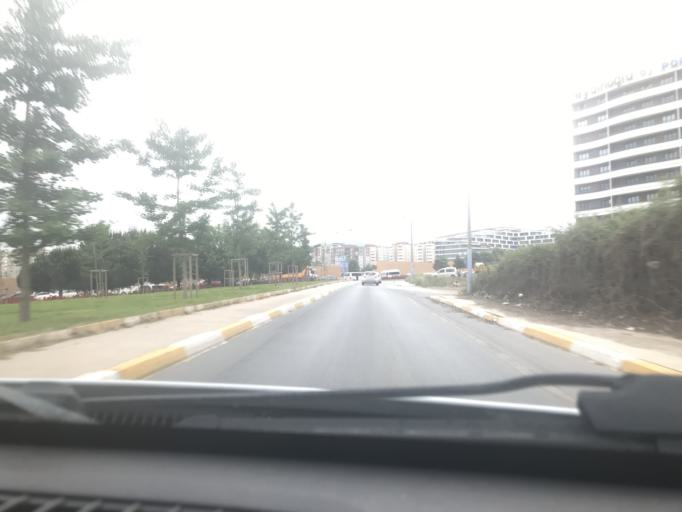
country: TR
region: Istanbul
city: Sultanbeyli
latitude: 40.9256
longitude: 29.3130
